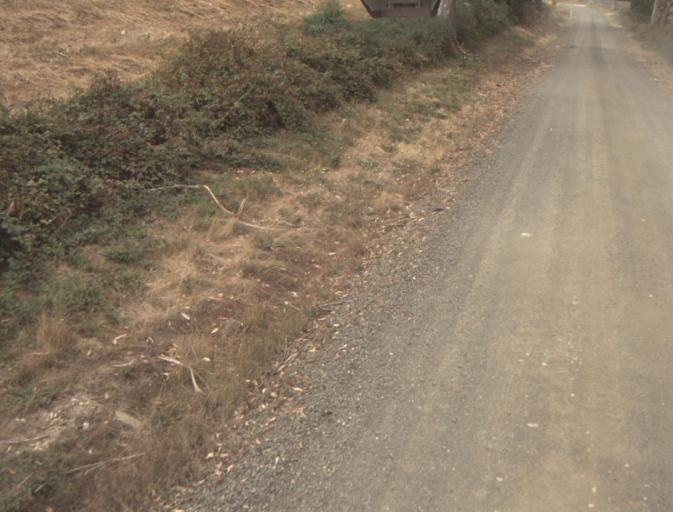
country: AU
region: Tasmania
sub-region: Dorset
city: Bridport
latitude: -41.1752
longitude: 147.2658
